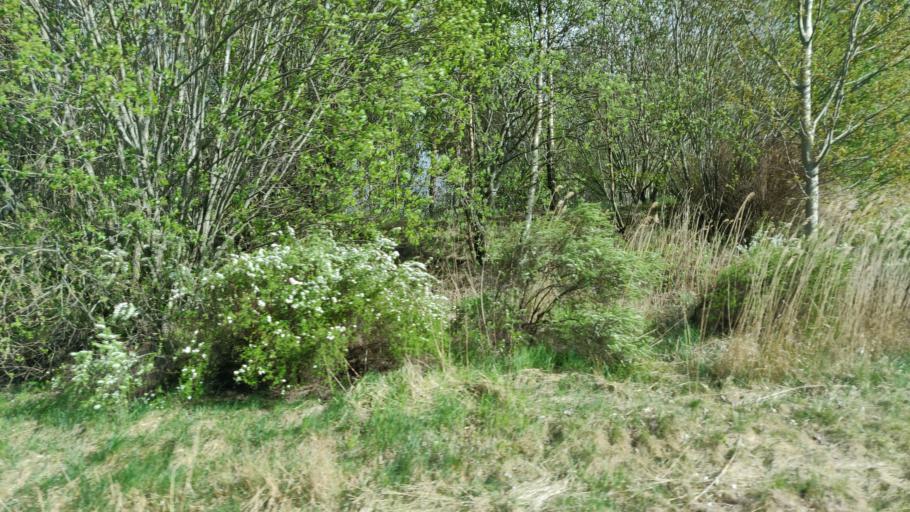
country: SE
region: Vaermland
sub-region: Hammaro Kommun
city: Skoghall
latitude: 59.3809
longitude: 13.4071
